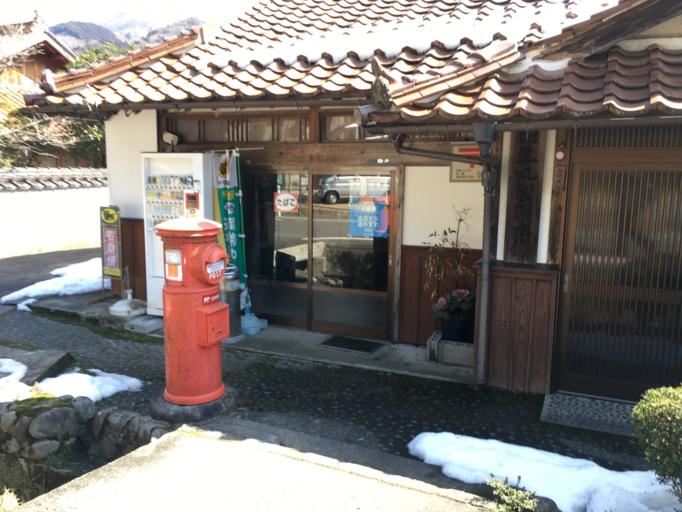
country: JP
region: Shimane
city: Masuda
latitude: 34.4550
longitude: 131.7656
